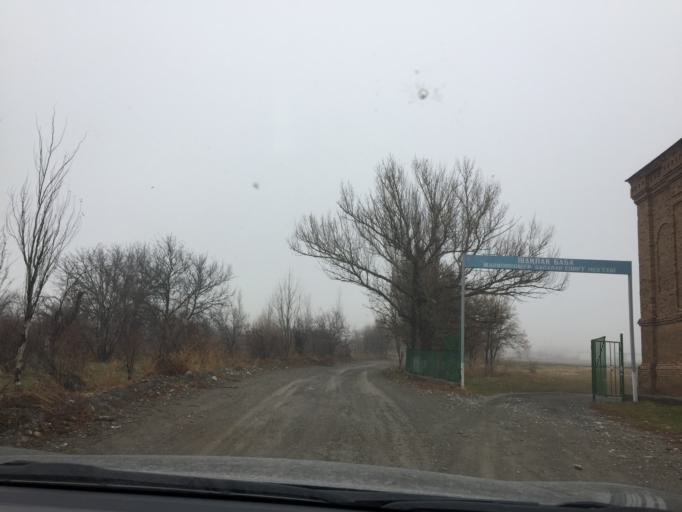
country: KZ
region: Ongtustik Qazaqstan
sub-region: Tulkibas Audany
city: Zhabagly
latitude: 42.5126
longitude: 70.5622
